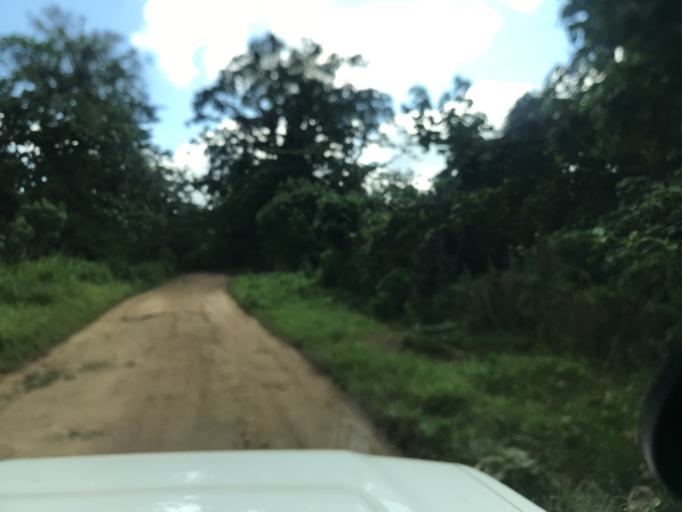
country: VU
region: Sanma
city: Luganville
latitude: -15.4907
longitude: 167.0896
